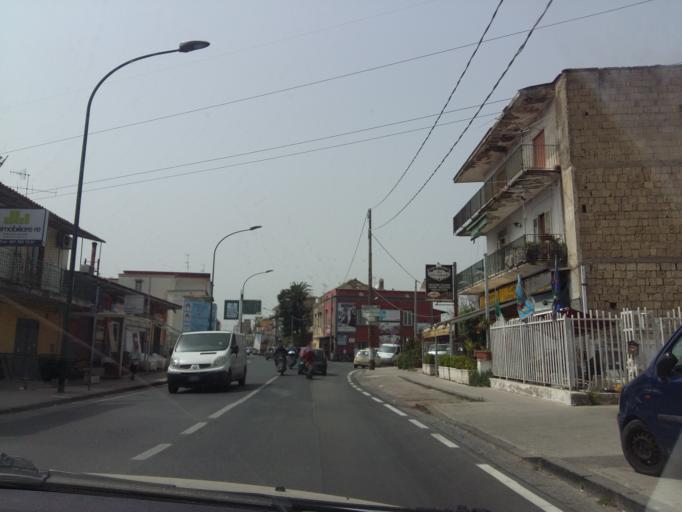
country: IT
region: Campania
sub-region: Provincia di Napoli
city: Mugnano di Napoli
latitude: 40.8980
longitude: 14.2102
